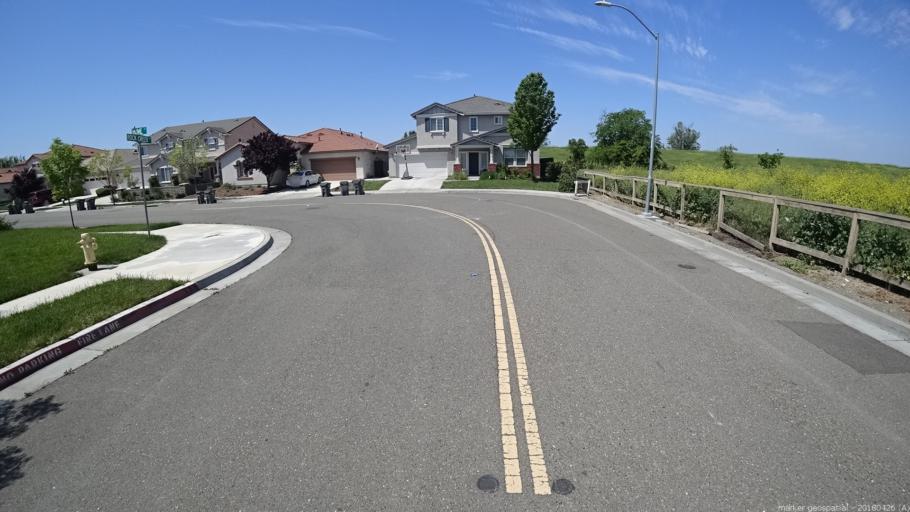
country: US
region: California
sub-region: Yolo County
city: West Sacramento
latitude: 38.5336
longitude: -121.5807
